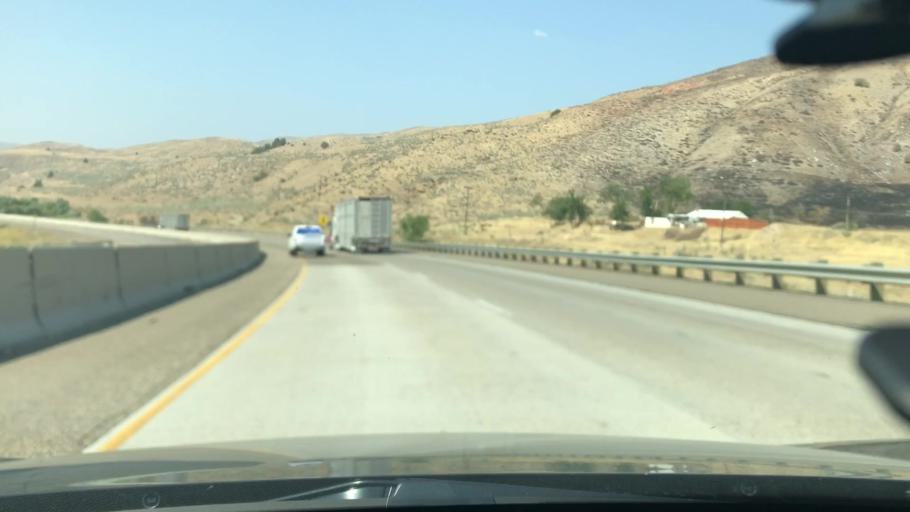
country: US
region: Idaho
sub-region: Washington County
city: Weiser
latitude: 44.4129
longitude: -117.3076
